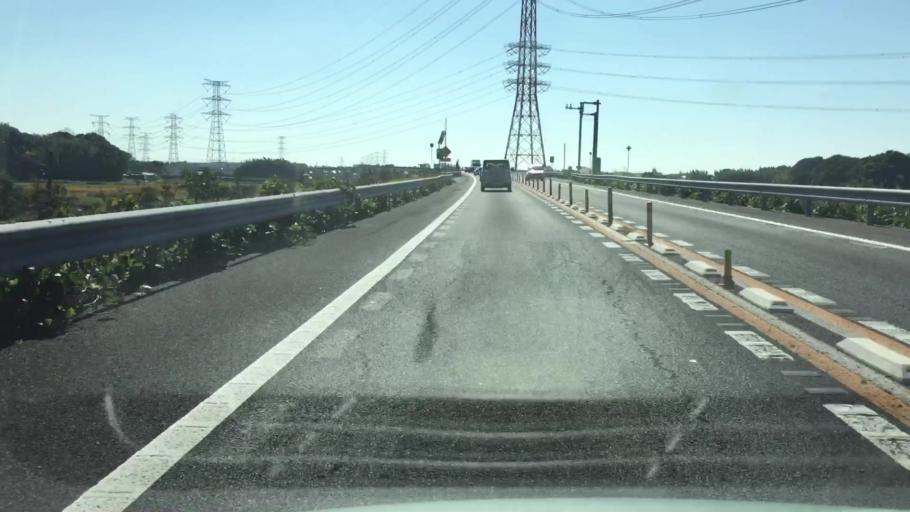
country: JP
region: Ibaraki
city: Ushiku
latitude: 36.0033
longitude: 140.1465
